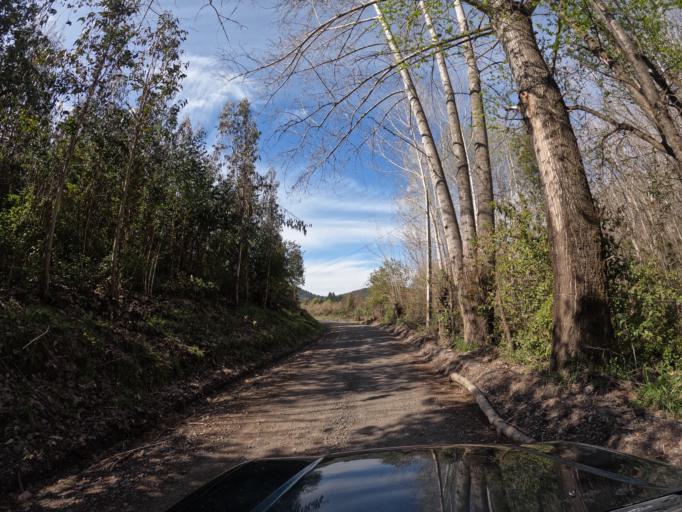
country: CL
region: Biobio
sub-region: Provincia de Concepcion
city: Chiguayante
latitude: -37.0682
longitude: -72.8994
